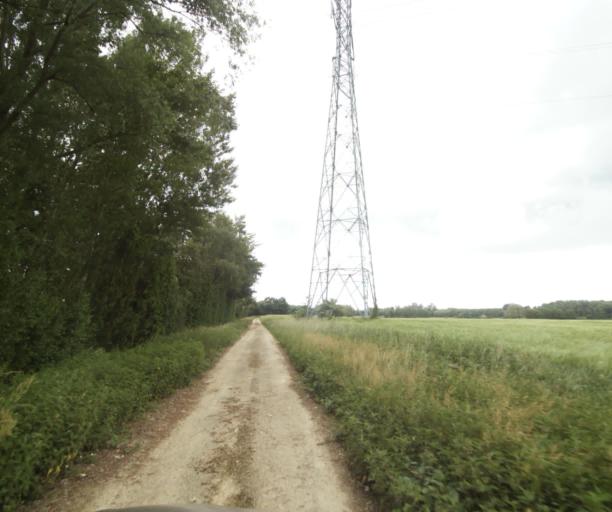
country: FR
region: Rhone-Alpes
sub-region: Departement de l'Ain
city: Tramoyes
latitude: 45.8578
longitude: 4.9531
